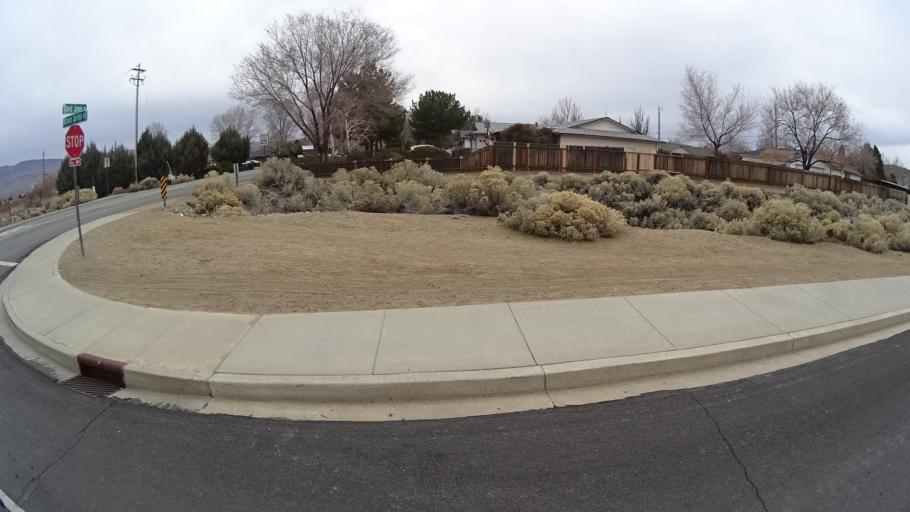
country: US
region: Nevada
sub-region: Washoe County
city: Spanish Springs
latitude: 39.6352
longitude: -119.7270
